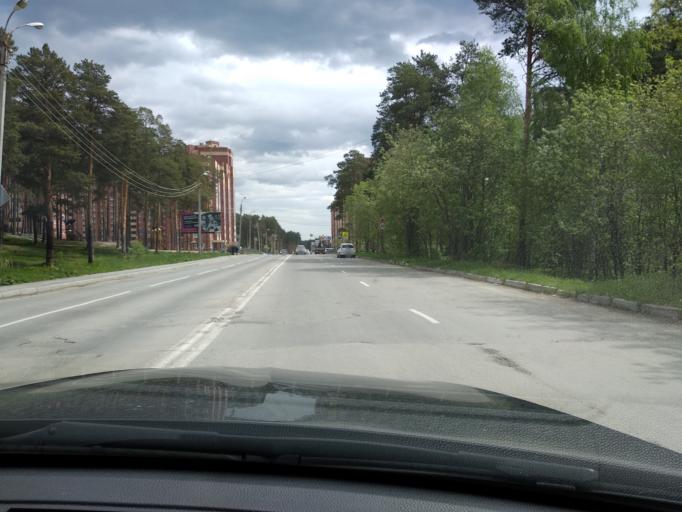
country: RU
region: Sverdlovsk
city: Beryozovsky
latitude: 56.9135
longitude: 60.8181
